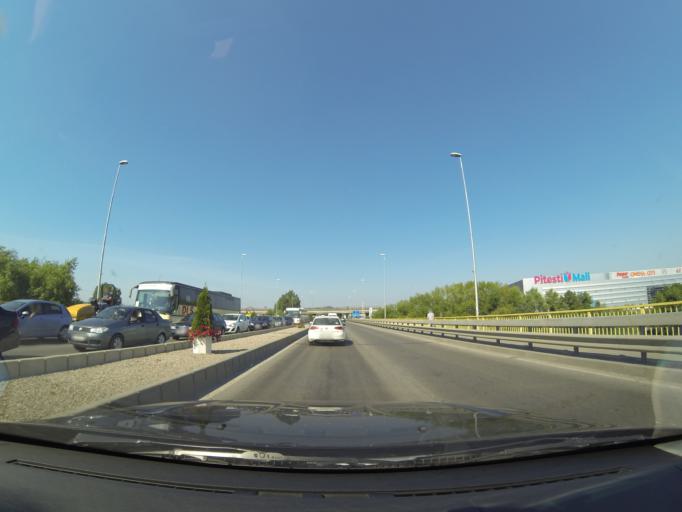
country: RO
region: Arges
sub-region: Comuna Albestii de Arges
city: Pitesti
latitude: 44.8661
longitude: 24.8808
